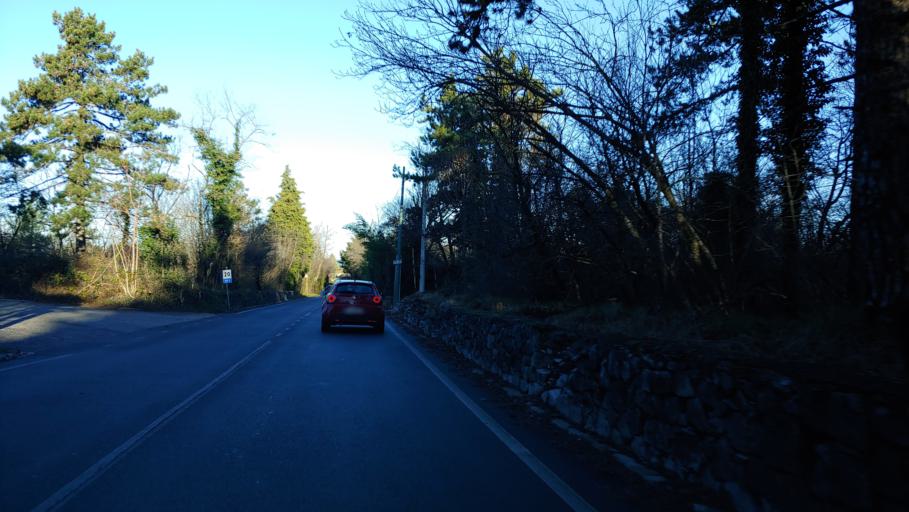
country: IT
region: Friuli Venezia Giulia
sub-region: Provincia di Trieste
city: Trieste
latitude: 45.6659
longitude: 13.8315
